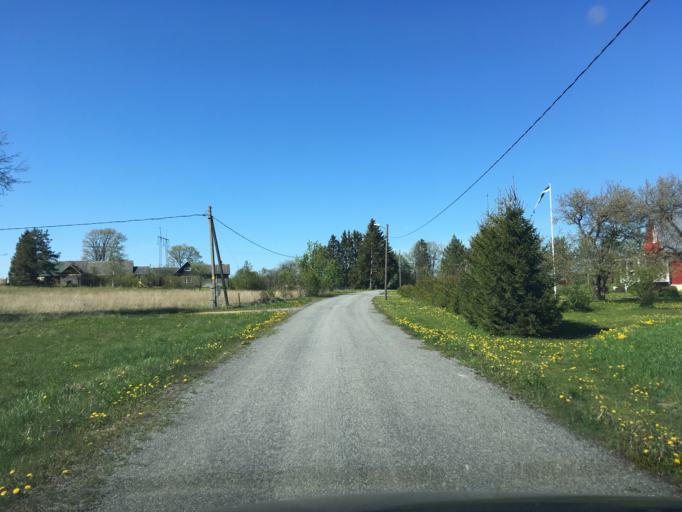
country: EE
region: Harju
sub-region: Raasiku vald
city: Arukula
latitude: 59.2693
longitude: 25.0944
